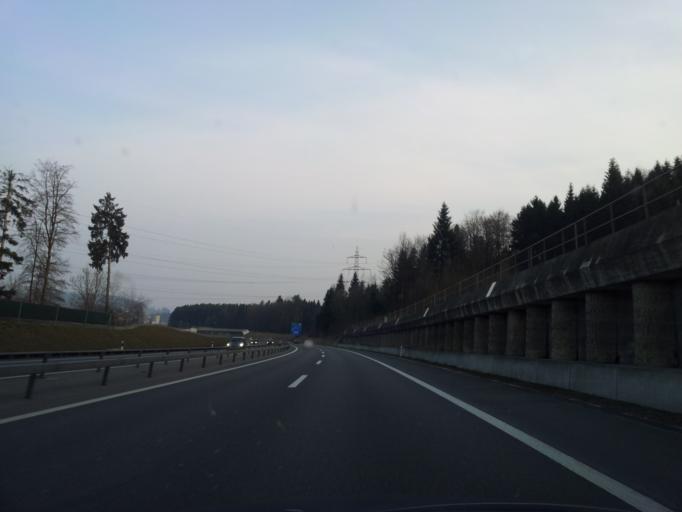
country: CH
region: Zurich
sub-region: Bezirk Affoltern
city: Obfelden / Toussen
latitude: 47.2799
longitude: 8.4275
